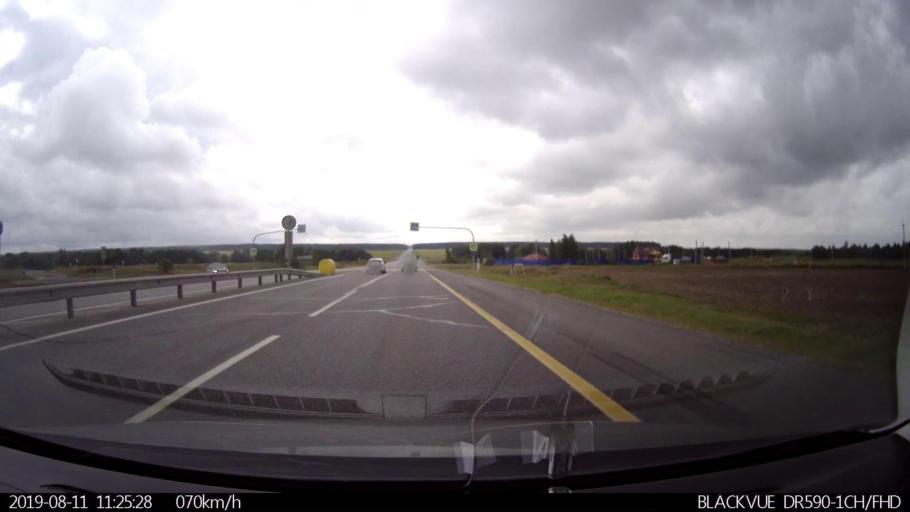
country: RU
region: Ulyanovsk
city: Krasnyy Gulyay
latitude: 54.1168
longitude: 48.2381
